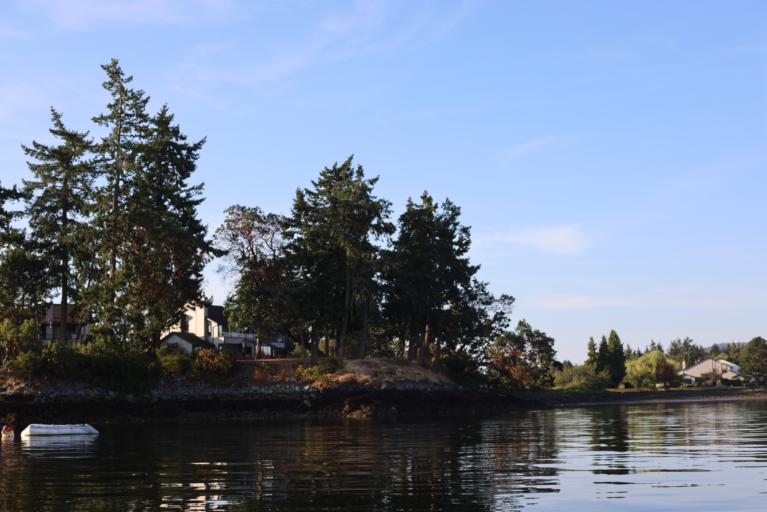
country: CA
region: British Columbia
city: North Saanich
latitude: 48.6705
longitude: -123.4103
